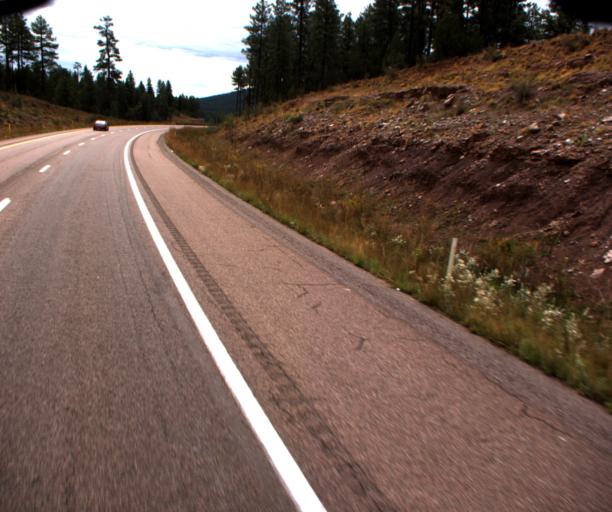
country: US
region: Arizona
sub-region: Gila County
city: Star Valley
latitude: 34.3116
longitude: -110.9996
